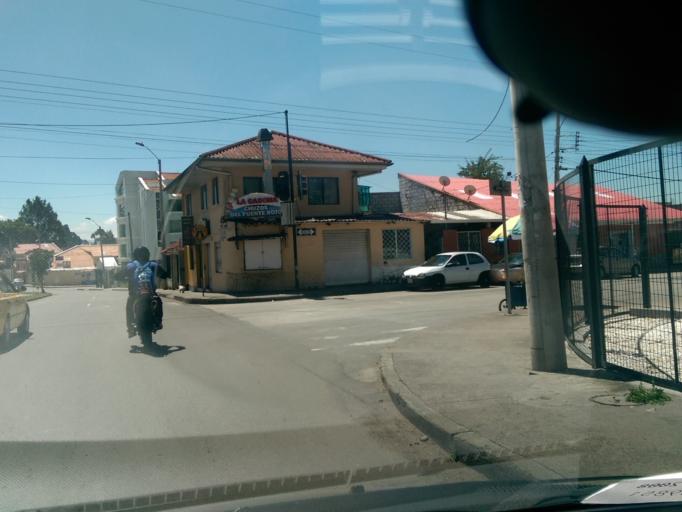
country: EC
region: Azuay
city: Cuenca
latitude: -2.9134
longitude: -79.0217
